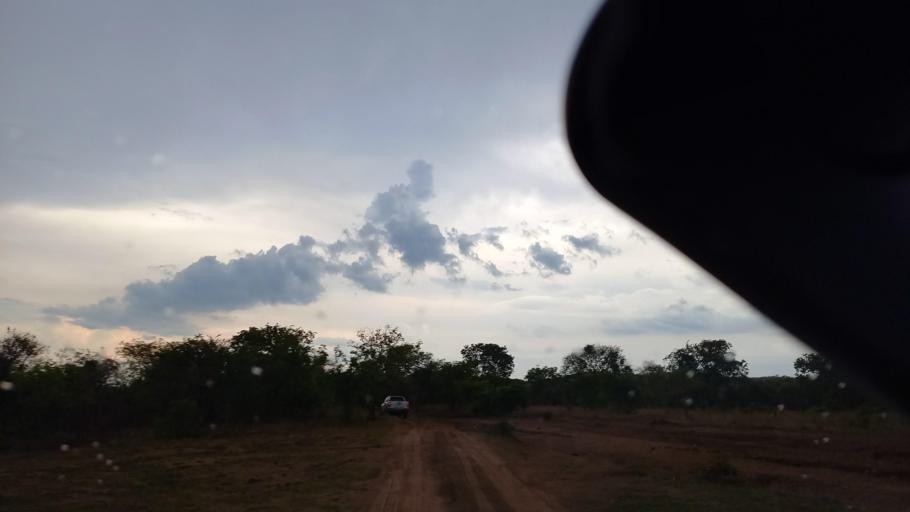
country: ZM
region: Lusaka
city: Kafue
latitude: -15.9774
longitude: 28.2550
